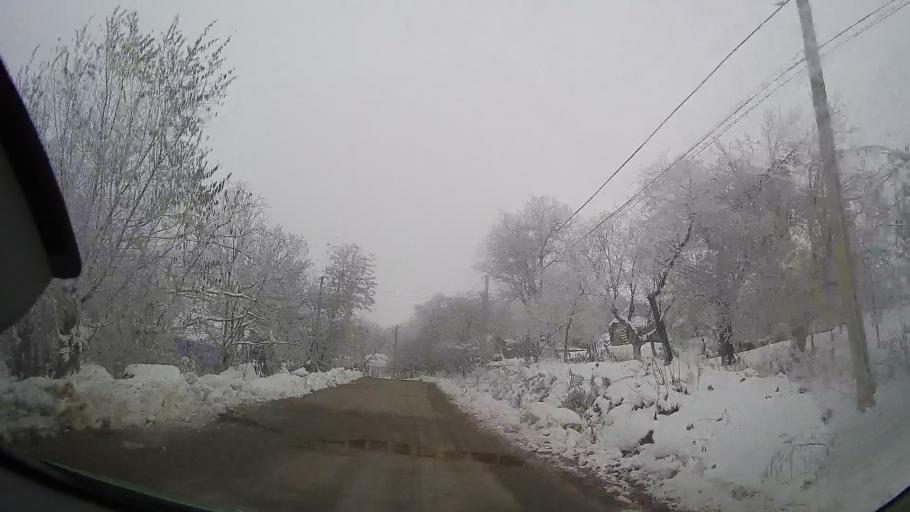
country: RO
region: Iasi
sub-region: Comuna Tansa
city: Suhulet
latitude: 46.8940
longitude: 27.2829
